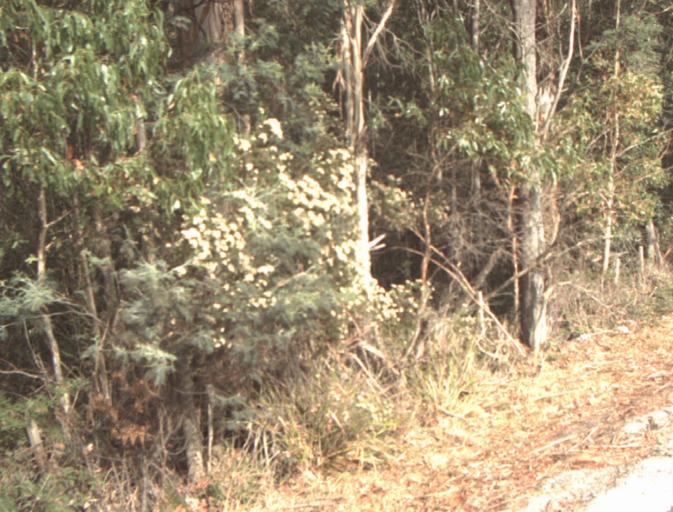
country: AU
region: Tasmania
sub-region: Launceston
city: Mayfield
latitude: -41.2740
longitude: 147.2177
